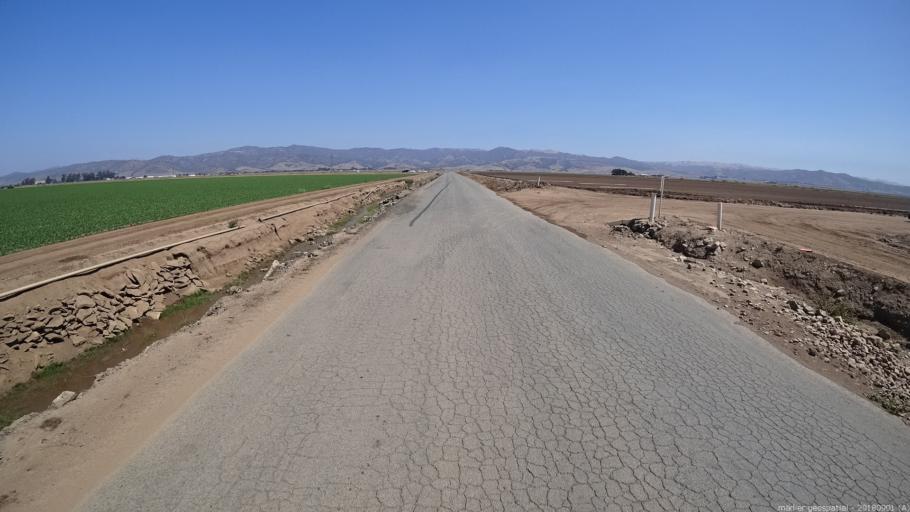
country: US
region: California
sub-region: Monterey County
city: Chualar
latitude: 36.5974
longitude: -121.5244
